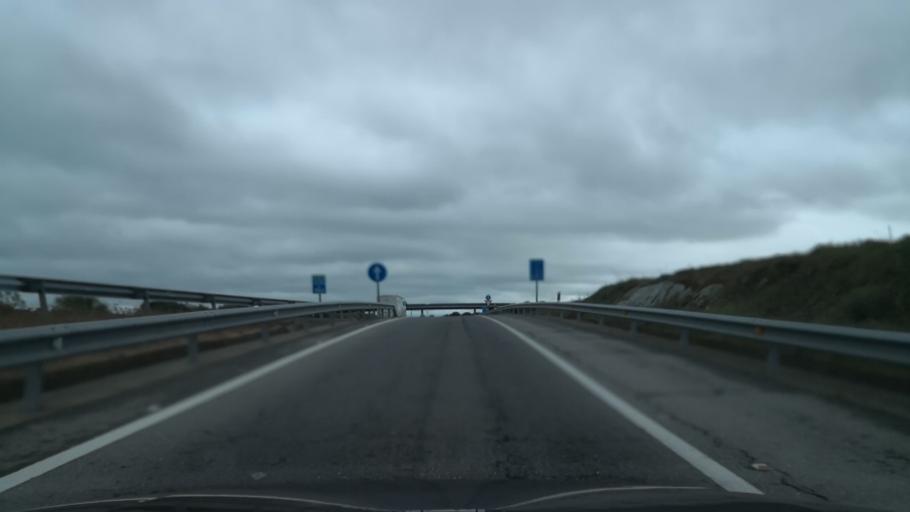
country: ES
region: Extremadura
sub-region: Provincia de Caceres
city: Caceres
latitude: 39.4597
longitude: -6.4213
